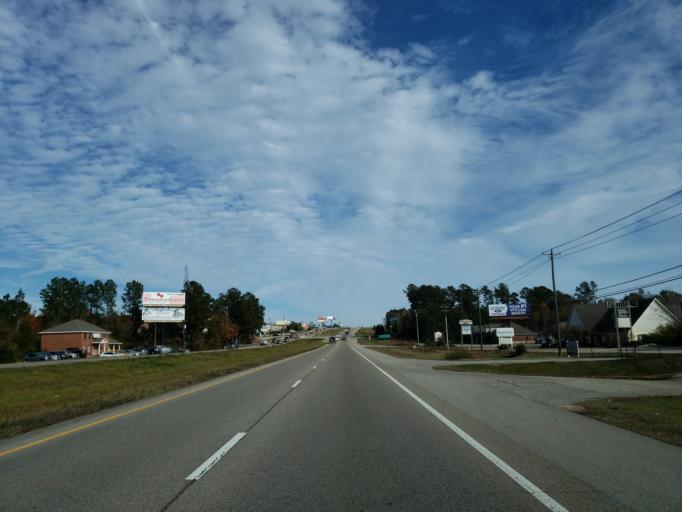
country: US
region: Mississippi
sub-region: Lamar County
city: West Hattiesburg
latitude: 31.3169
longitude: -89.4247
